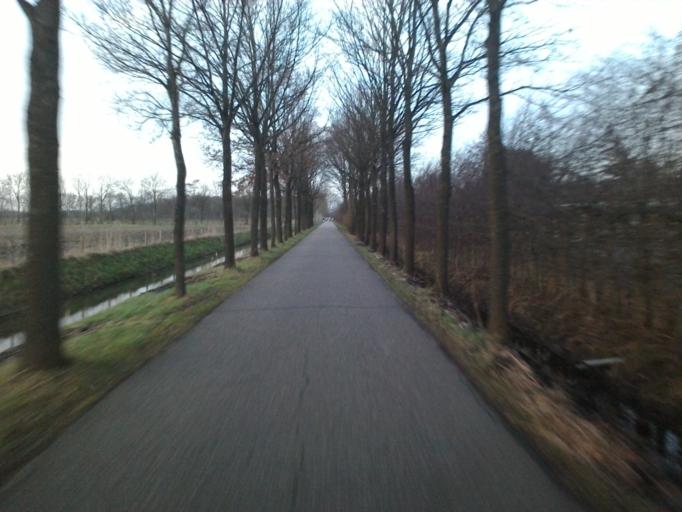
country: NL
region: Utrecht
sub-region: Gemeente Bunnik
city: Bunnik
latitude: 52.0817
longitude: 5.1941
